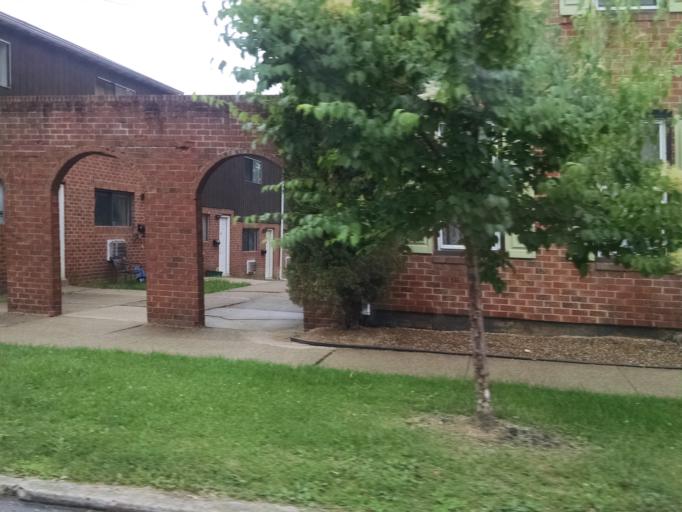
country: US
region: Pennsylvania
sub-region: Indiana County
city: Indiana
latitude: 40.6252
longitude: -79.1456
